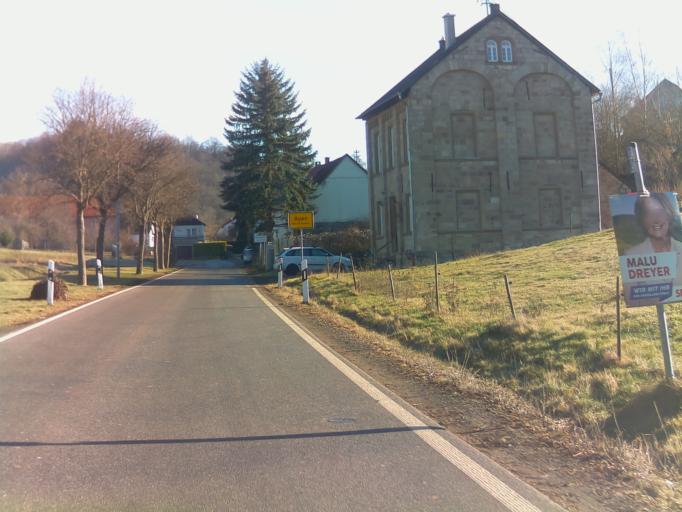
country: DE
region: Rheinland-Pfalz
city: Auen
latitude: 49.8299
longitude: 7.5937
